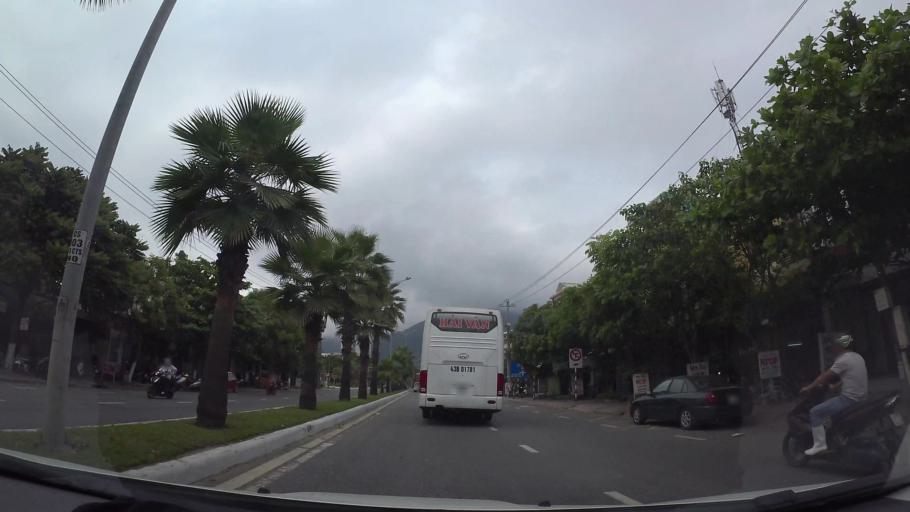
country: VN
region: Da Nang
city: Da Nang
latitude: 16.1049
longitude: 108.2469
